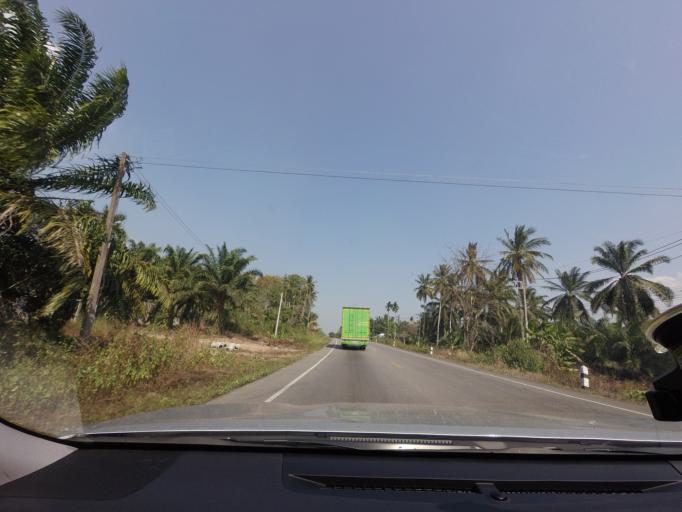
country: TH
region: Krabi
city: Plai Phraya
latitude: 8.5562
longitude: 98.8008
